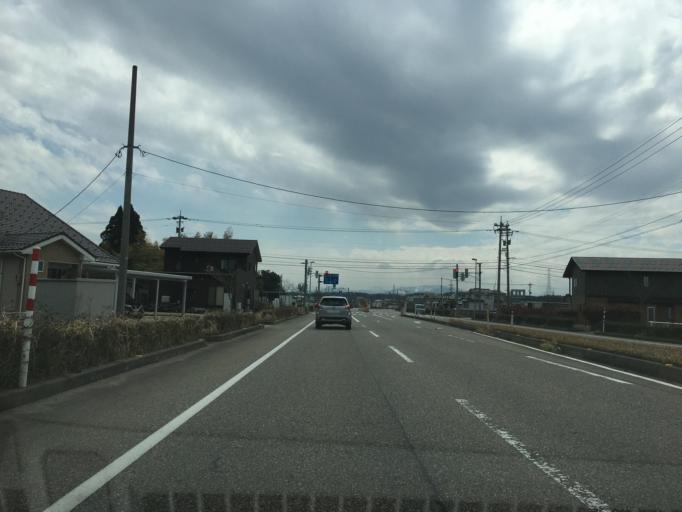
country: JP
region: Toyama
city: Kuragaki-kosugi
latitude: 36.7042
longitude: 137.1150
